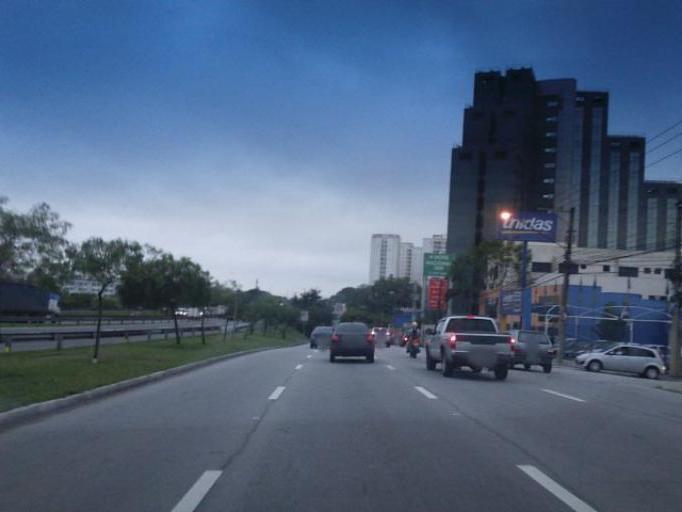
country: BR
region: Sao Paulo
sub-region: Sao Jose Dos Campos
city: Sao Jose dos Campos
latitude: -23.2025
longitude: -45.8820
